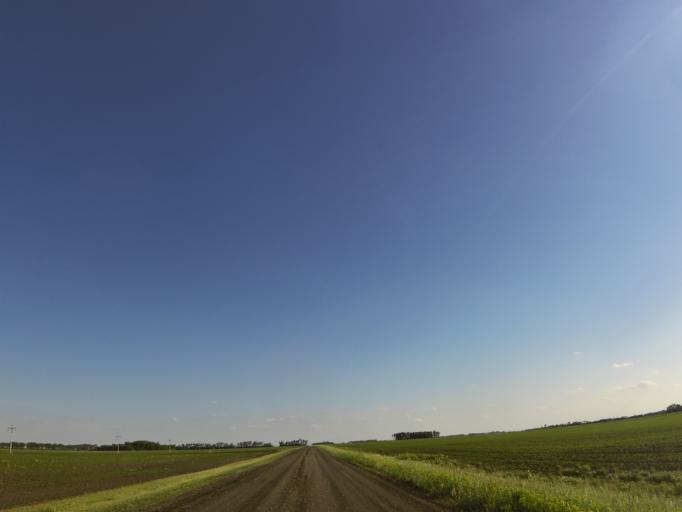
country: US
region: North Dakota
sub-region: Walsh County
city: Grafton
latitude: 48.4072
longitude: -97.2340
